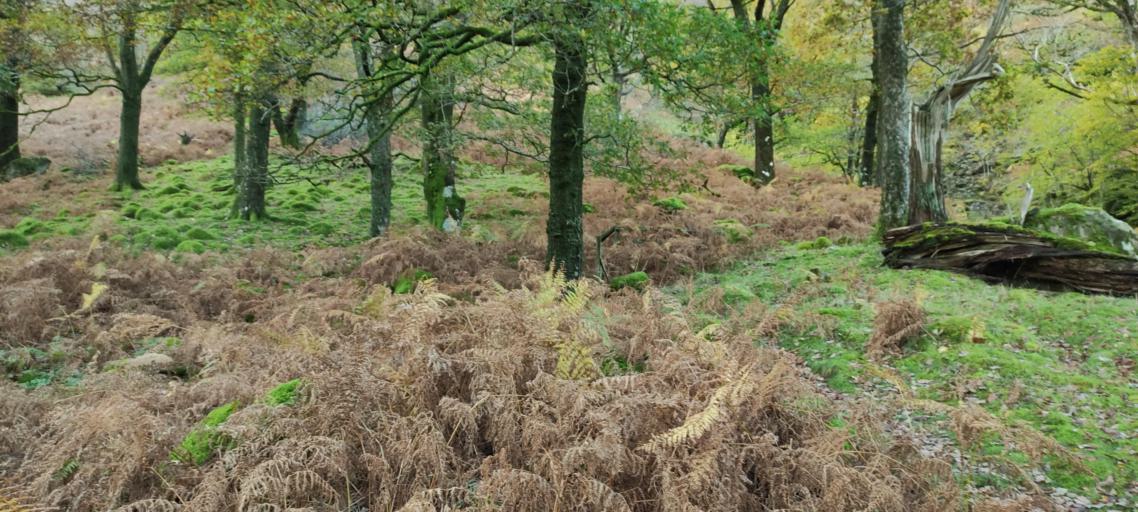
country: GB
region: England
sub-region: Cumbria
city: Keswick
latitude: 54.5091
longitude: -3.1366
